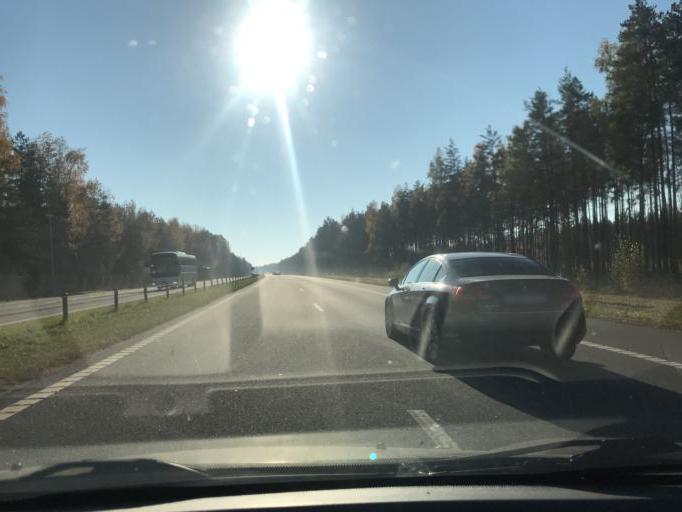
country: BY
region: Minsk
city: Pukhavichy
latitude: 53.4833
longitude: 28.3661
